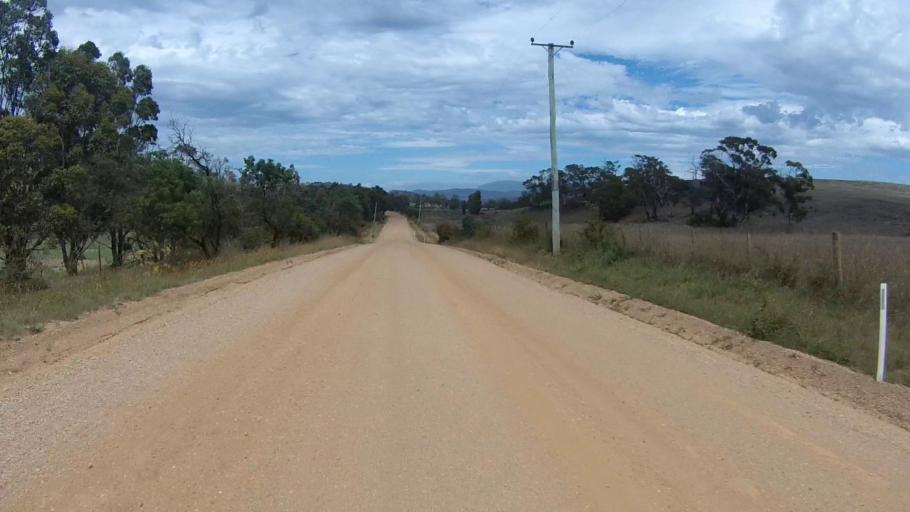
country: AU
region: Tasmania
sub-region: Sorell
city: Sorell
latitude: -42.6929
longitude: 147.4651
